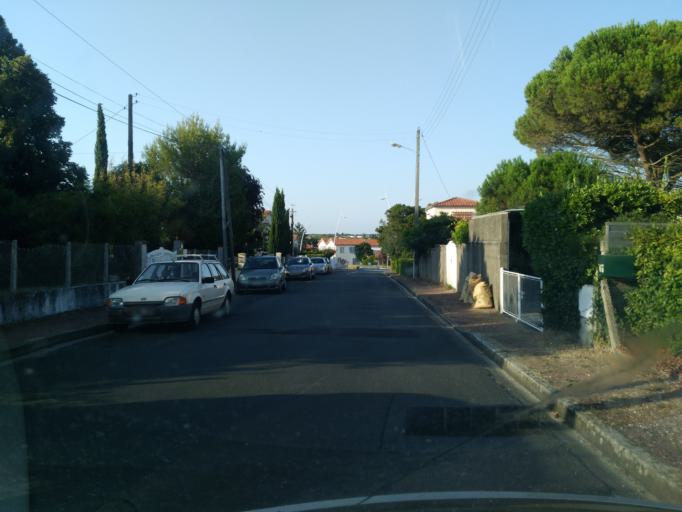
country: FR
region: Poitou-Charentes
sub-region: Departement de la Charente-Maritime
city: Vaux-sur-Mer
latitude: 45.6363
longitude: -1.0603
